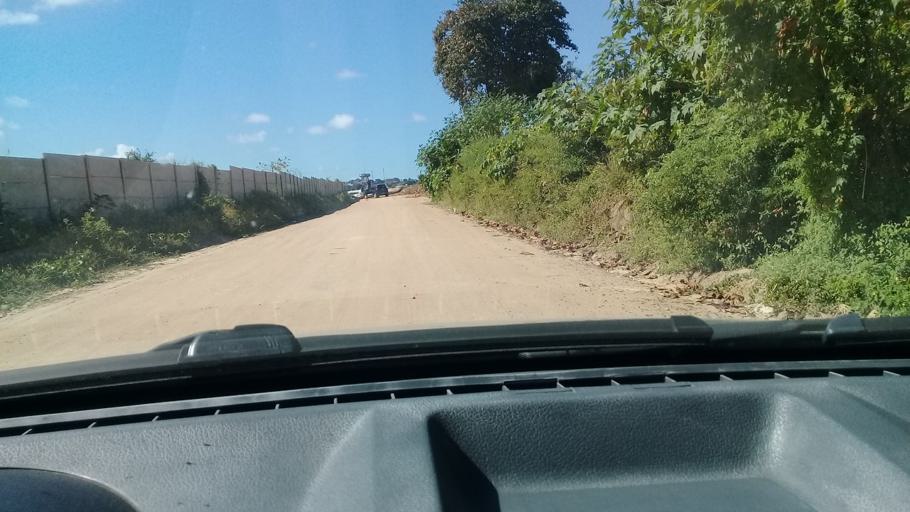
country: BR
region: Pernambuco
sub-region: Jaboatao Dos Guararapes
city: Jaboatao
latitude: -8.1520
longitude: -34.9504
